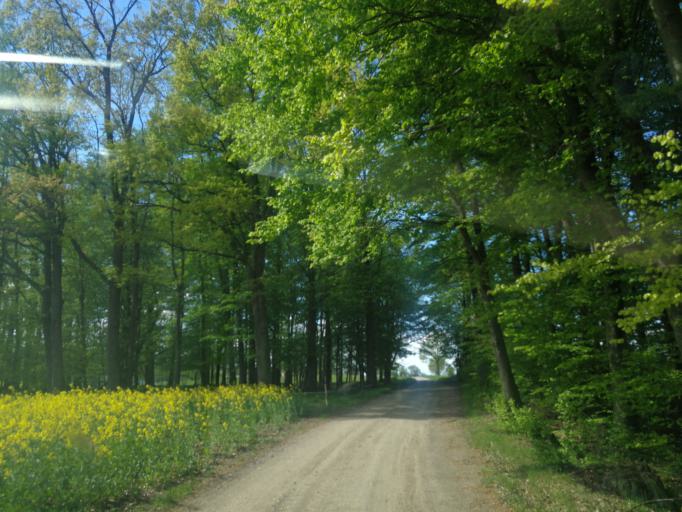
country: PL
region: Warmian-Masurian Voivodeship
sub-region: Powiat ilawski
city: Zalewo
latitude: 53.7595
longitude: 19.6775
